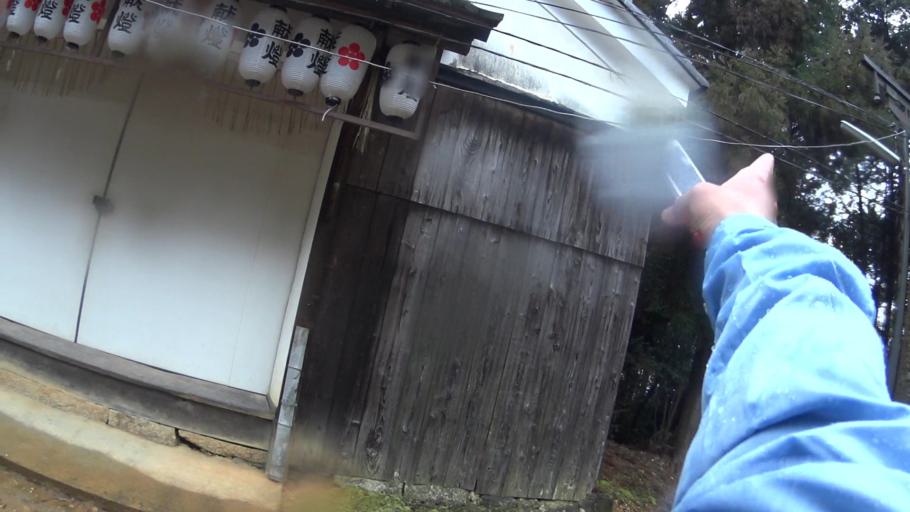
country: JP
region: Kyoto
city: Uji
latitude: 34.9540
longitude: 135.8224
